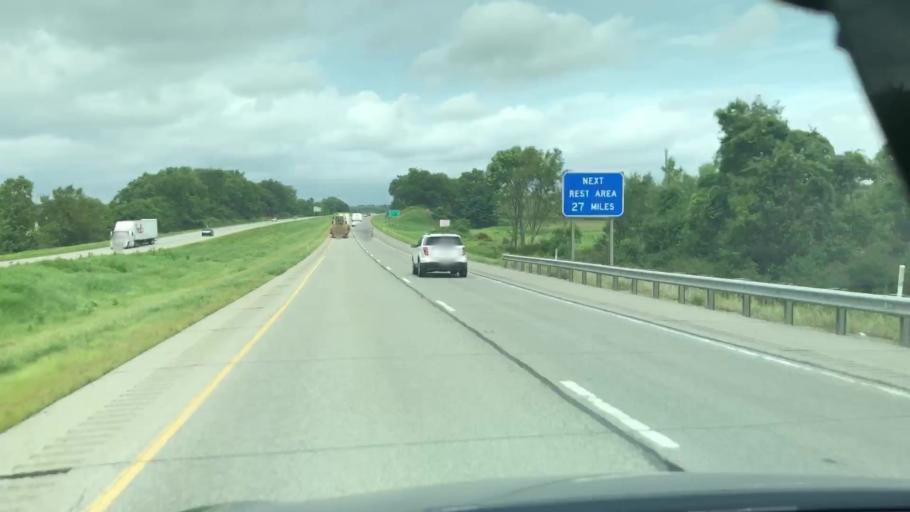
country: US
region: Pennsylvania
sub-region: Butler County
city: Slippery Rock
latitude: 41.0481
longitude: -80.1267
